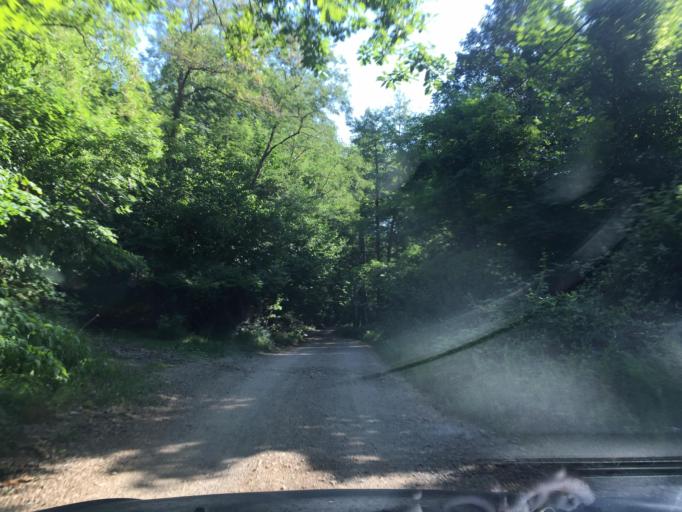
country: HR
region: Primorsko-Goranska
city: Klana
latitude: 45.4351
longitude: 14.3917
